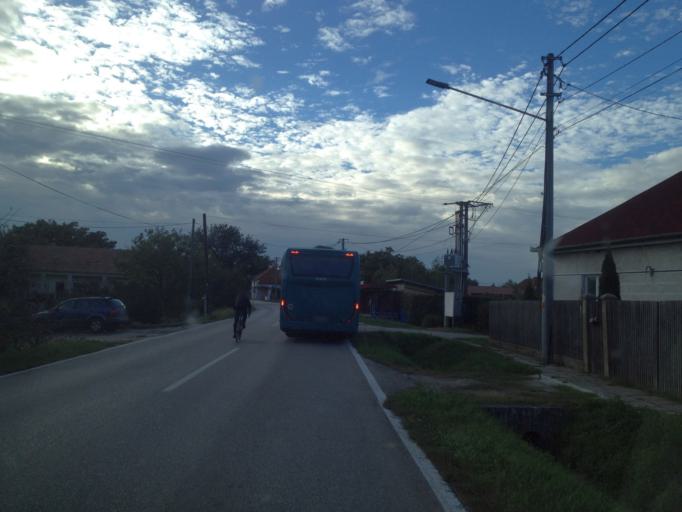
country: HU
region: Komarom-Esztergom
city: Almasfuzito
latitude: 47.7486
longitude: 18.2323
